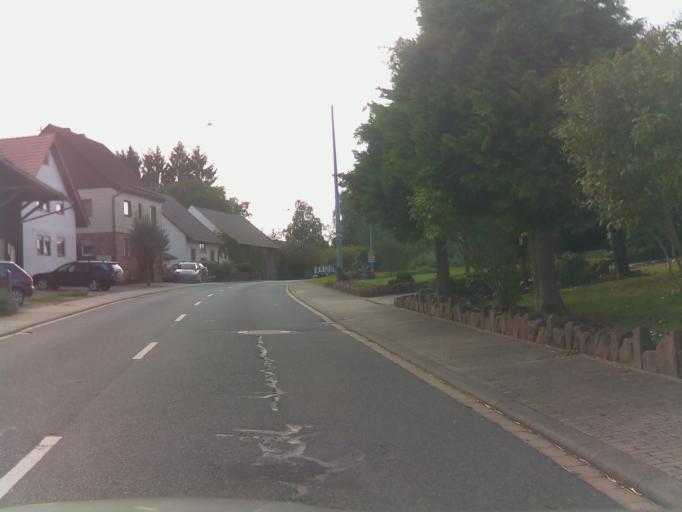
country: DE
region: Baden-Wuerttemberg
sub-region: Karlsruhe Region
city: Mudau
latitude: 49.5410
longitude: 9.1456
